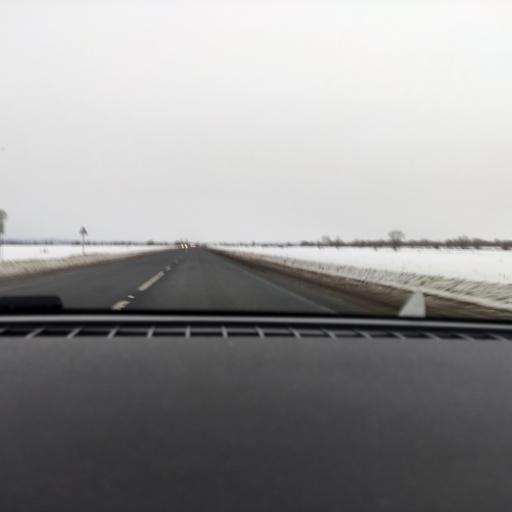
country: RU
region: Samara
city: Kinel'
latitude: 53.1547
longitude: 50.5136
